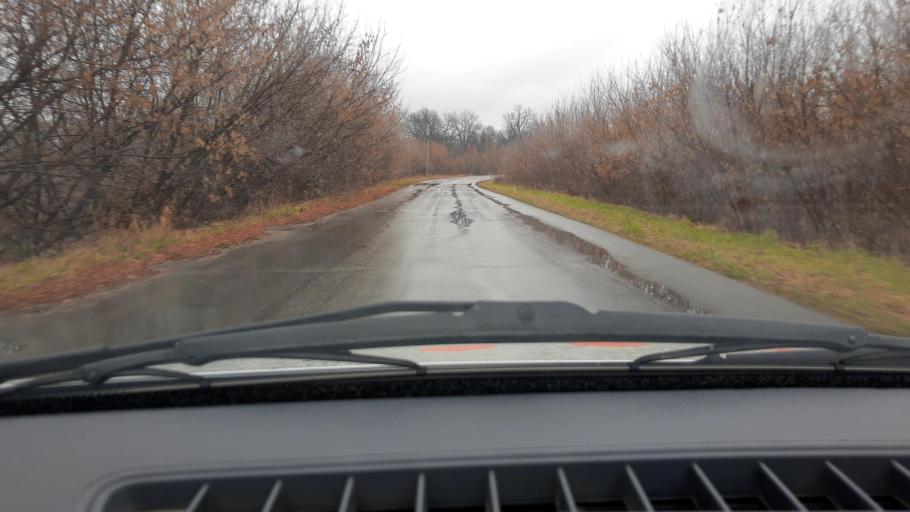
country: RU
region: Bashkortostan
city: Iglino
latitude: 54.8073
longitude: 56.1907
